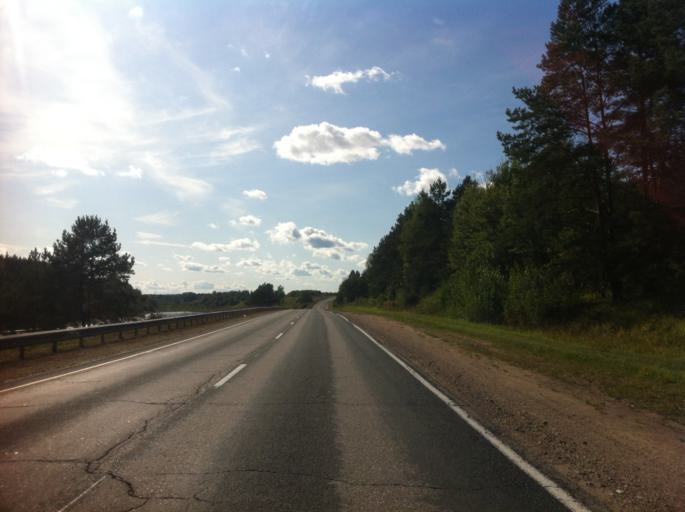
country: RU
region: Pskov
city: Izborsk
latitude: 57.7495
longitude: 27.7453
